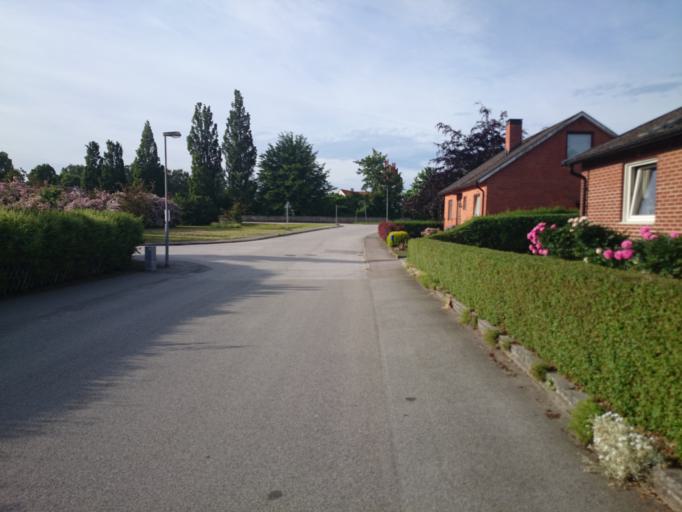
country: SE
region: Skane
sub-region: Eslovs Kommun
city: Eslov
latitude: 55.7236
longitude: 13.3405
